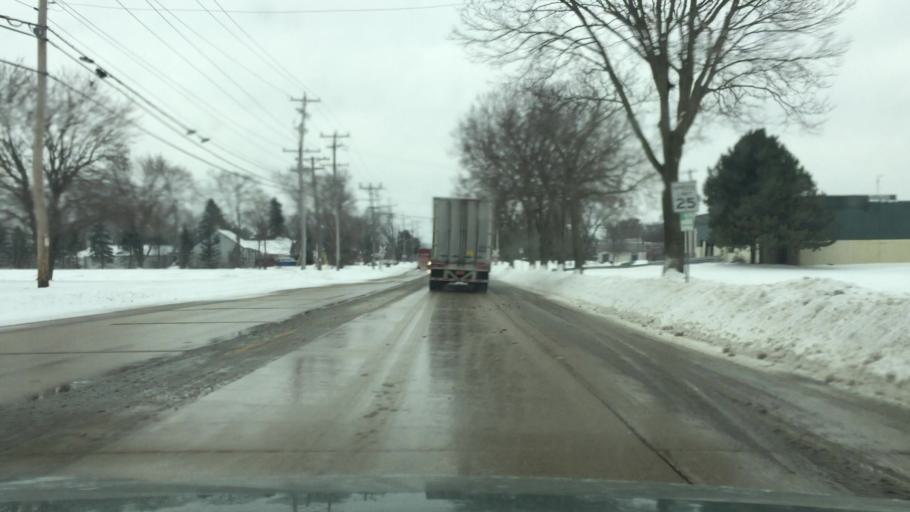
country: US
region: Wisconsin
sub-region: Waukesha County
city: Waukesha
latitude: 42.9911
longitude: -88.2434
